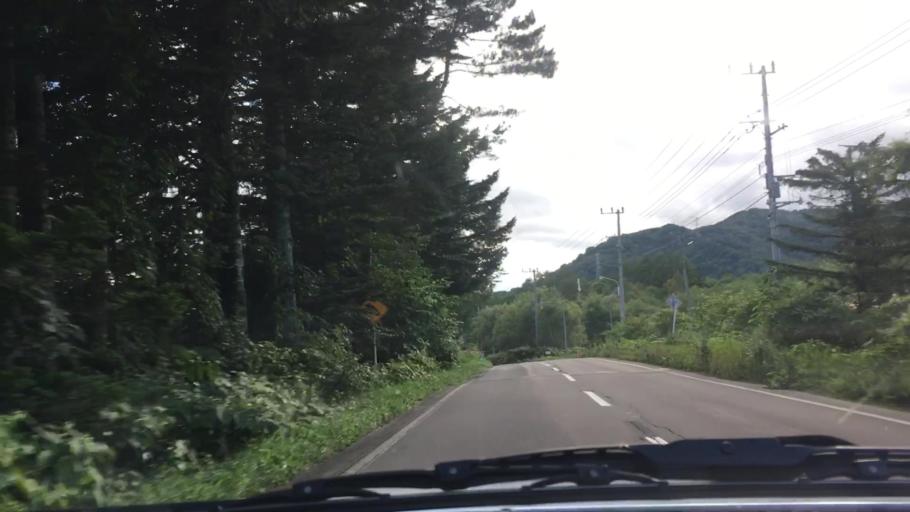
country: JP
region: Hokkaido
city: Otofuke
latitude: 43.1735
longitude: 142.9179
